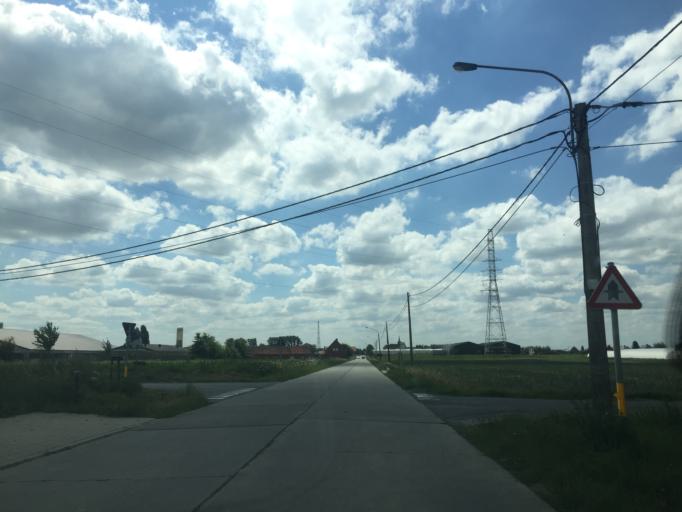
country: BE
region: Flanders
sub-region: Provincie West-Vlaanderen
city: Staden
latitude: 50.9544
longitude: 2.9881
